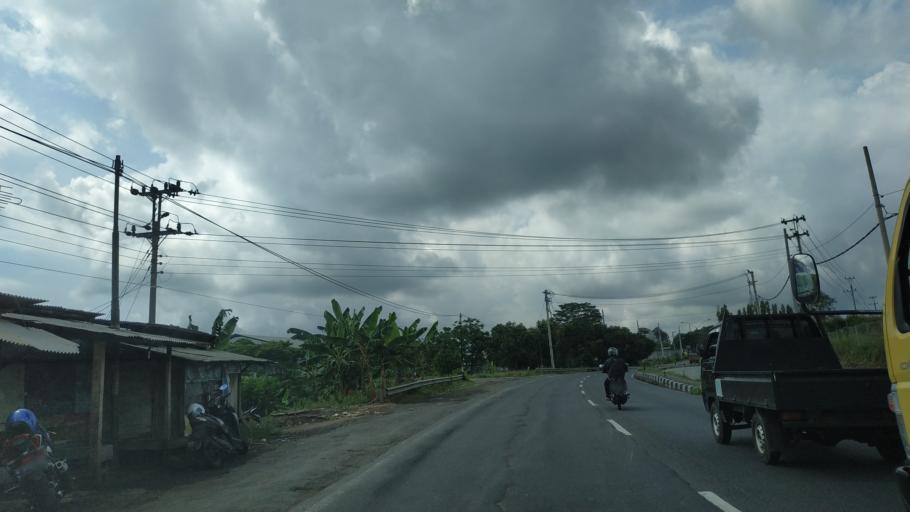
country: ID
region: Central Java
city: Pekalongan
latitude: -6.9467
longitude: 109.8242
